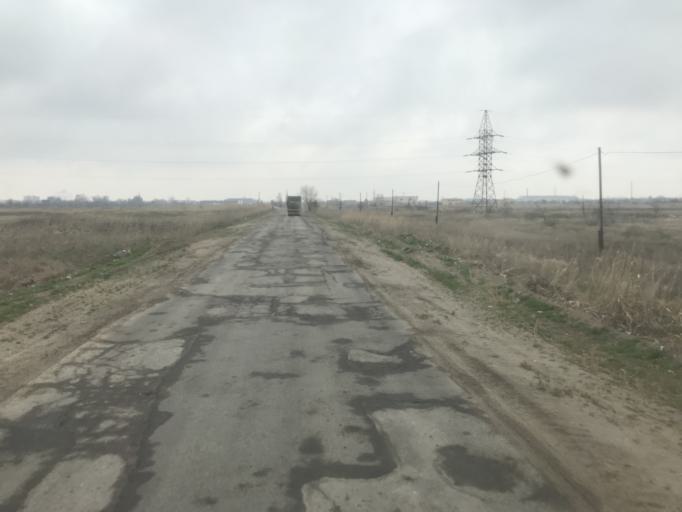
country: RU
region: Volgograd
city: Svetlyy Yar
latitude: 48.5175
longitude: 44.6284
